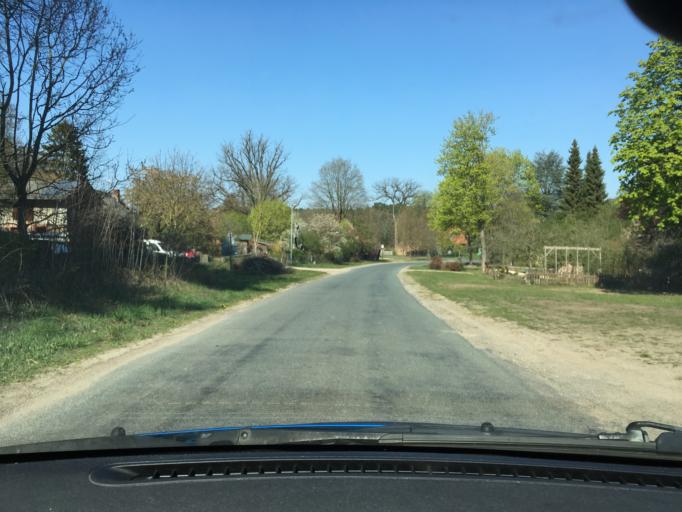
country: DE
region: Lower Saxony
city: Hitzacker
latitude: 53.1251
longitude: 11.0132
